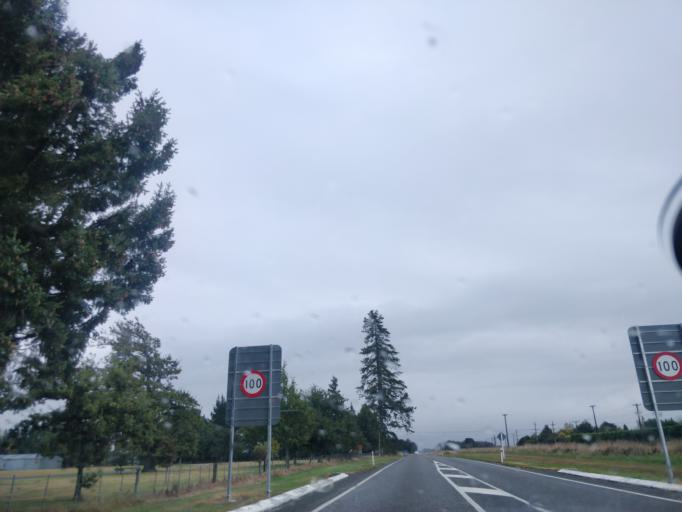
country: NZ
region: Canterbury
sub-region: Selwyn District
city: Darfield
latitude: -43.3855
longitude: 172.0136
